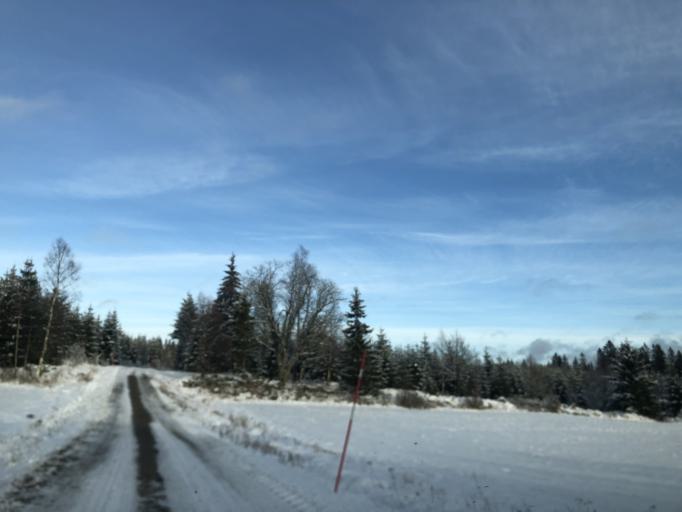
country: SE
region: Vaestra Goetaland
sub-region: Ulricehamns Kommun
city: Ulricehamn
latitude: 57.7424
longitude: 13.4999
